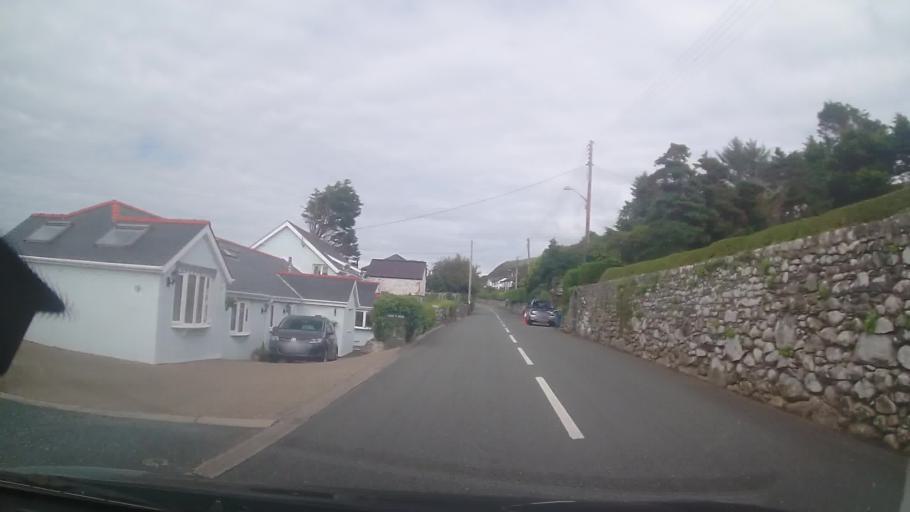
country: GB
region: Wales
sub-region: Gwynedd
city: Barmouth
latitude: 52.6728
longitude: -4.0807
